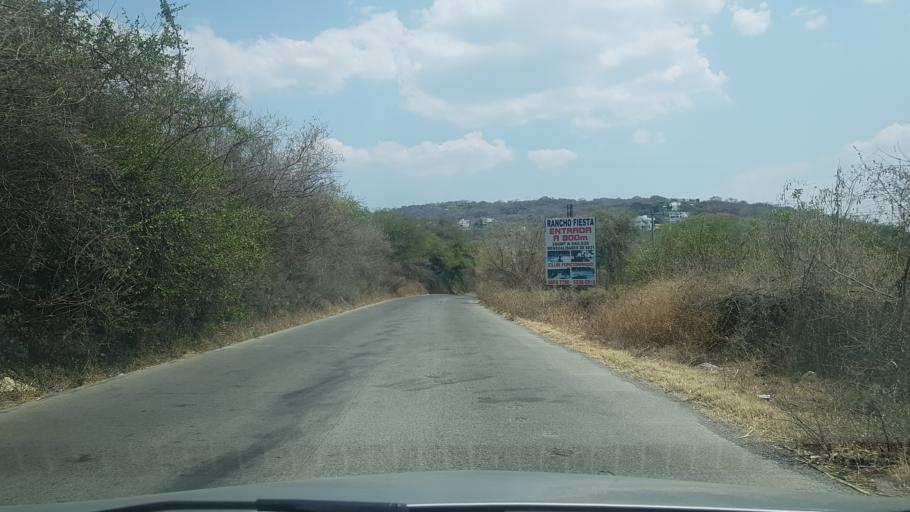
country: MX
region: Morelos
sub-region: Tlaltizapan de Zapata
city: Colonia Palo Prieto (Chipitongo)
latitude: 18.7475
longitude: -99.1128
